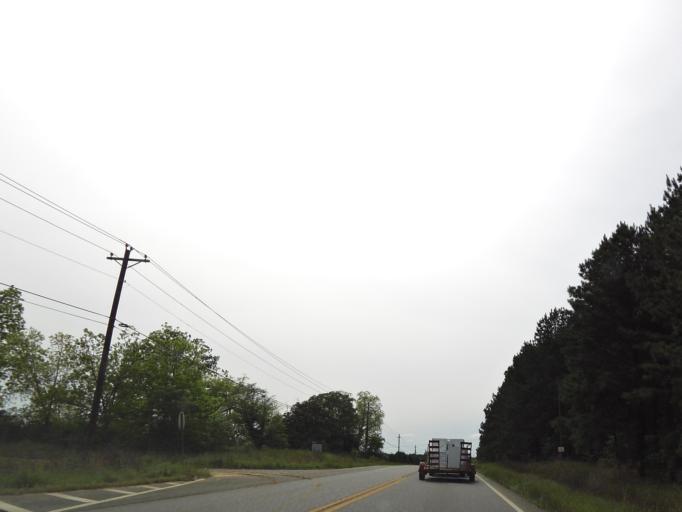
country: US
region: Georgia
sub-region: Houston County
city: Robins Air Force Base
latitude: 32.5437
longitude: -83.5769
